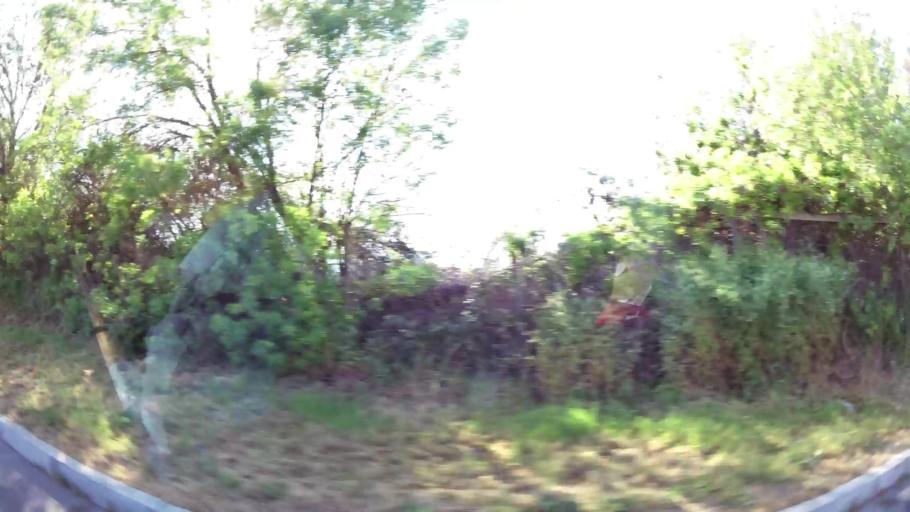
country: CL
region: Santiago Metropolitan
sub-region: Provincia de Chacabuco
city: Chicureo Abajo
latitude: -33.3604
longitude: -70.6642
